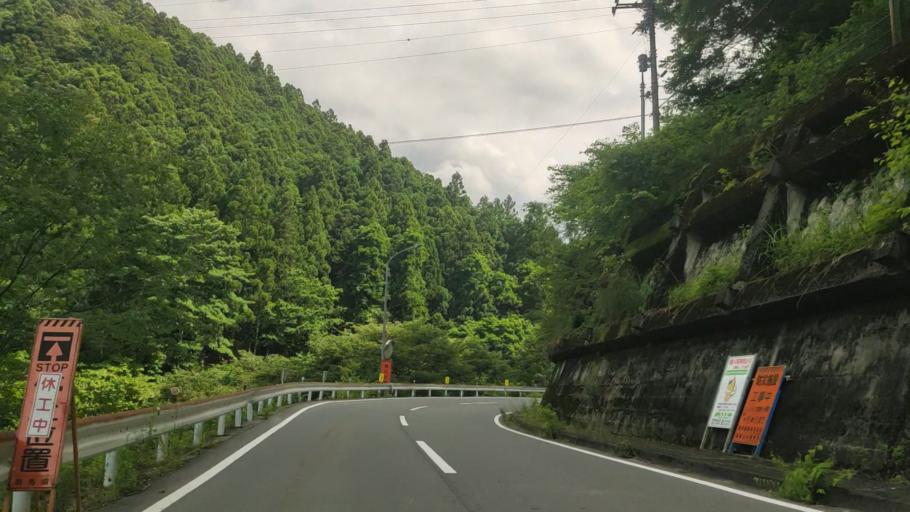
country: JP
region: Gunma
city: Tomioka
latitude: 36.1640
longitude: 138.7297
